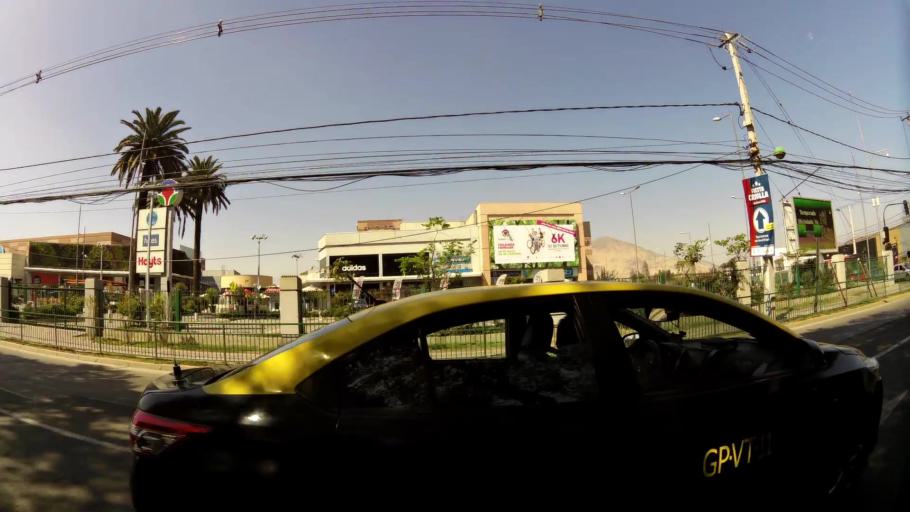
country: CL
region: Santiago Metropolitan
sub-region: Provincia de Santiago
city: Lo Prado
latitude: -33.3682
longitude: -70.7313
